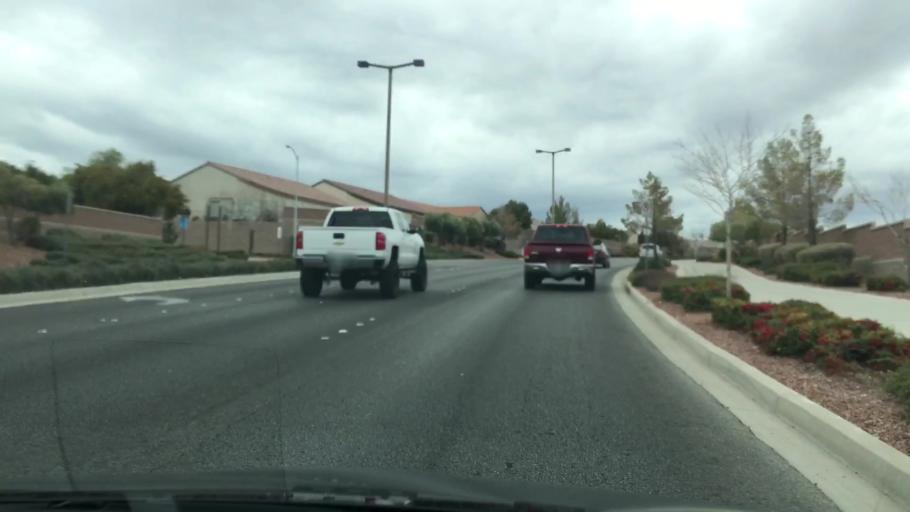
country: US
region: Nevada
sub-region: Clark County
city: Whitney
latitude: 35.9507
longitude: -115.0923
